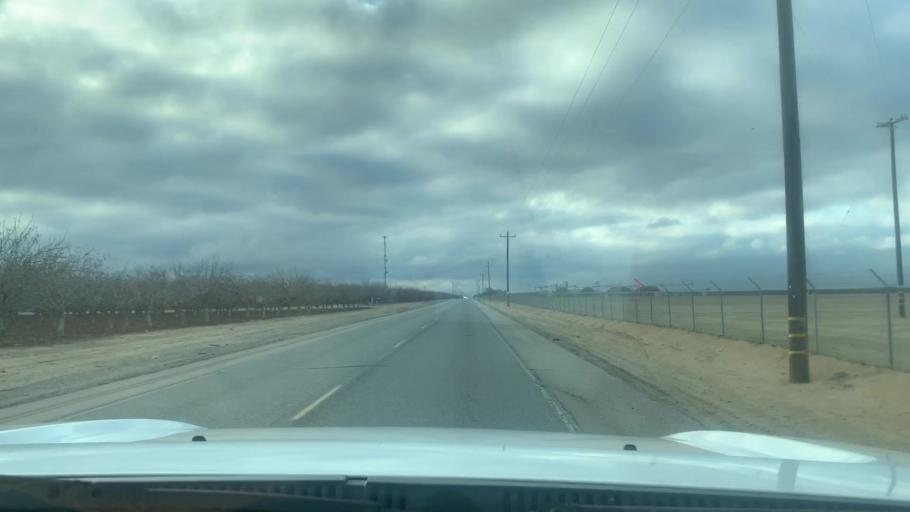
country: US
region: California
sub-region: Kern County
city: Buttonwillow
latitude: 35.5007
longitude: -119.4956
